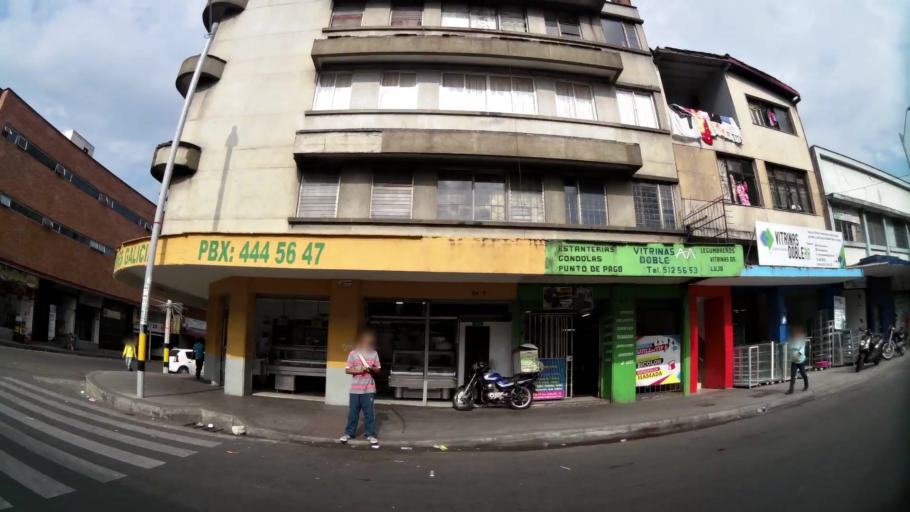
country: CO
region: Antioquia
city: Medellin
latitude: 6.2547
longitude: -75.5692
